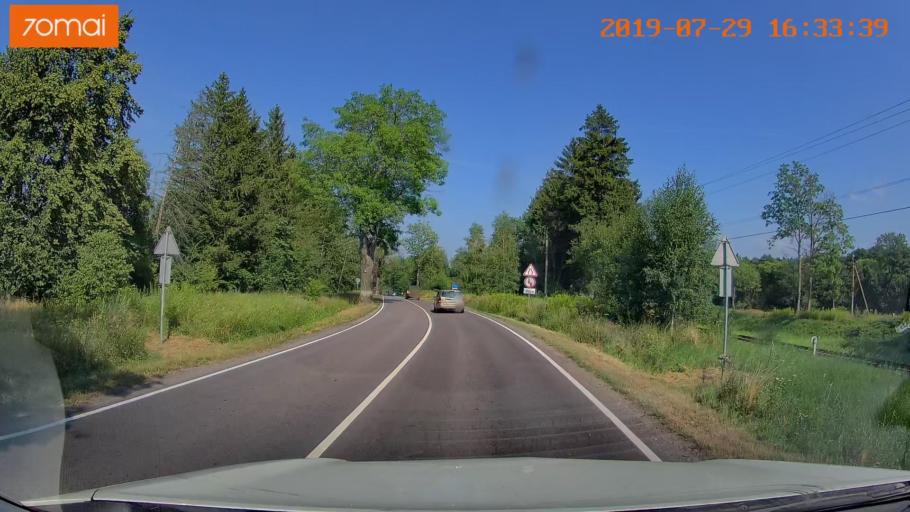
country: RU
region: Kaliningrad
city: Primorsk
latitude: 54.7387
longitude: 20.0390
